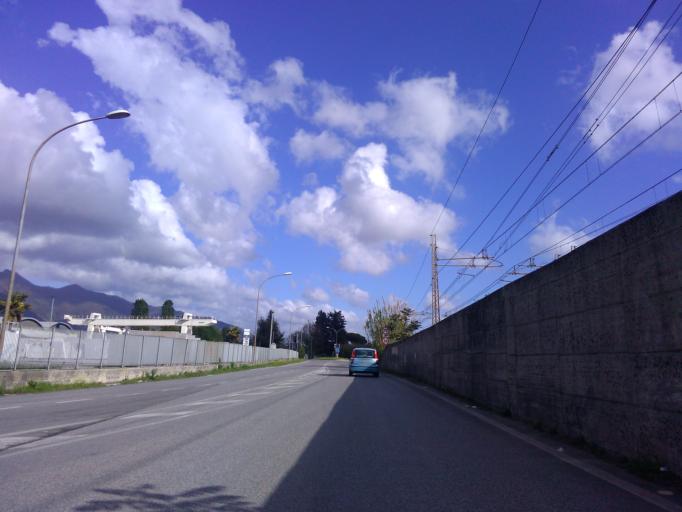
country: IT
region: Tuscany
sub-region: Provincia di Lucca
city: Strettoia
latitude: 43.9908
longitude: 10.1816
